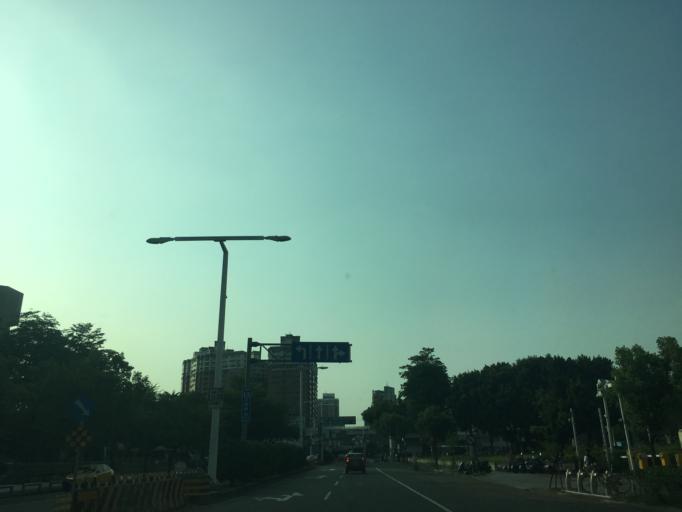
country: TW
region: Taiwan
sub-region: Taichung City
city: Taichung
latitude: 24.1272
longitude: 120.6697
